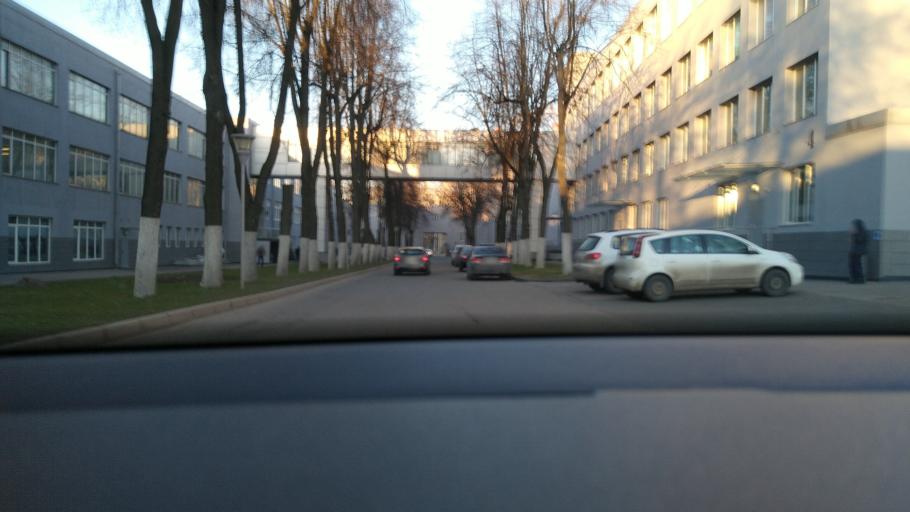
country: RU
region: Moskovskaya
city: Bol'shaya Setun'
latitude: 55.7124
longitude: 37.4180
